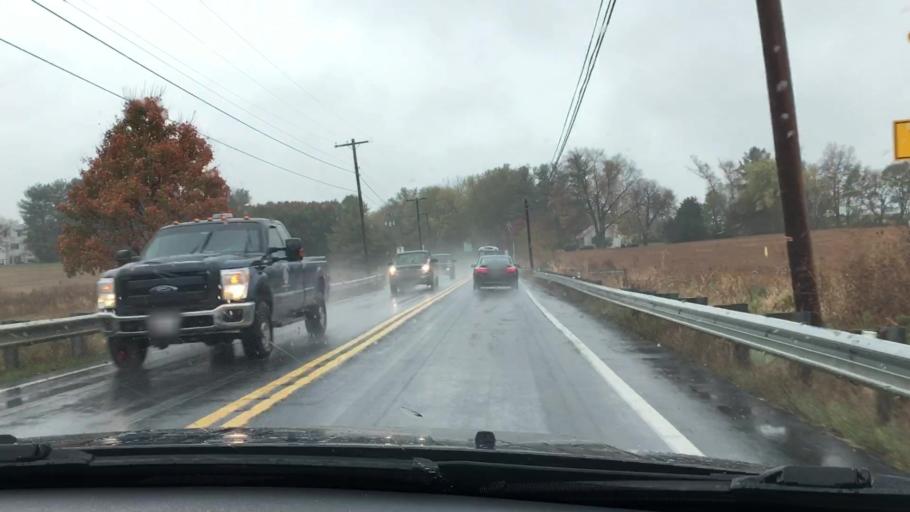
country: US
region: Maryland
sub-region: Frederick County
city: Adamstown
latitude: 39.2636
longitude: -77.4653
